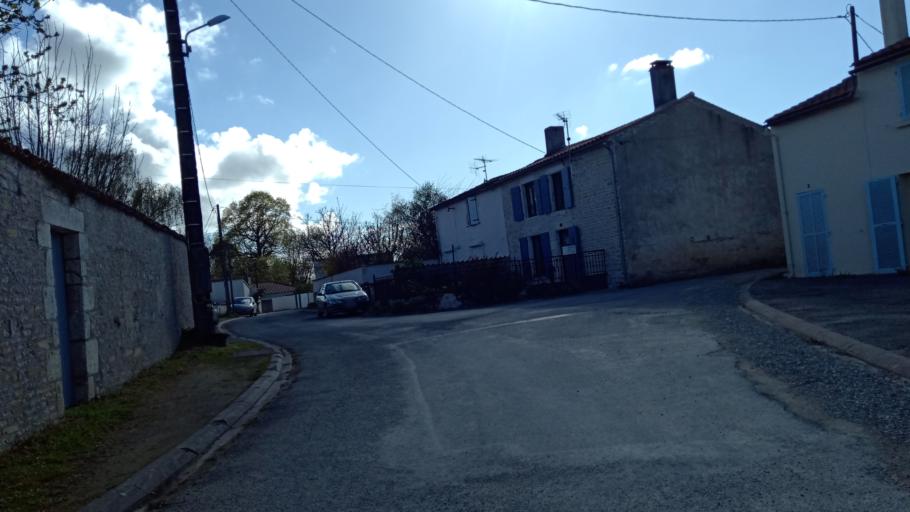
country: FR
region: Poitou-Charentes
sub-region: Departement de la Charente-Maritime
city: Verines
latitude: 46.1674
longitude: -0.9440
